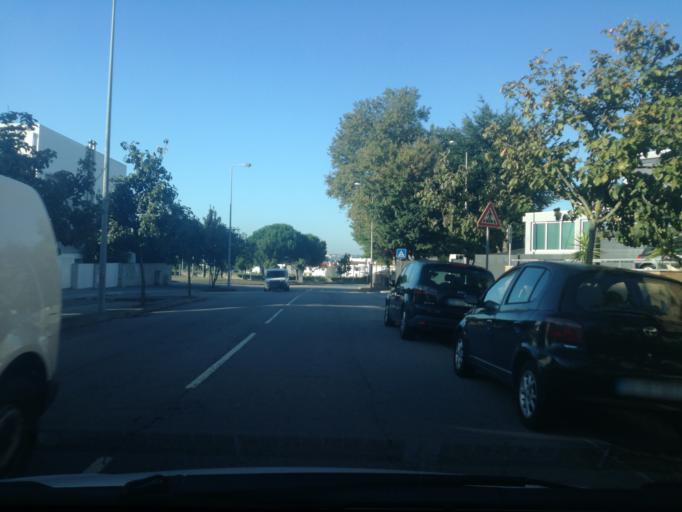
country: PT
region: Porto
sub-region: Maia
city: Milheiros
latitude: 41.2185
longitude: -8.5878
